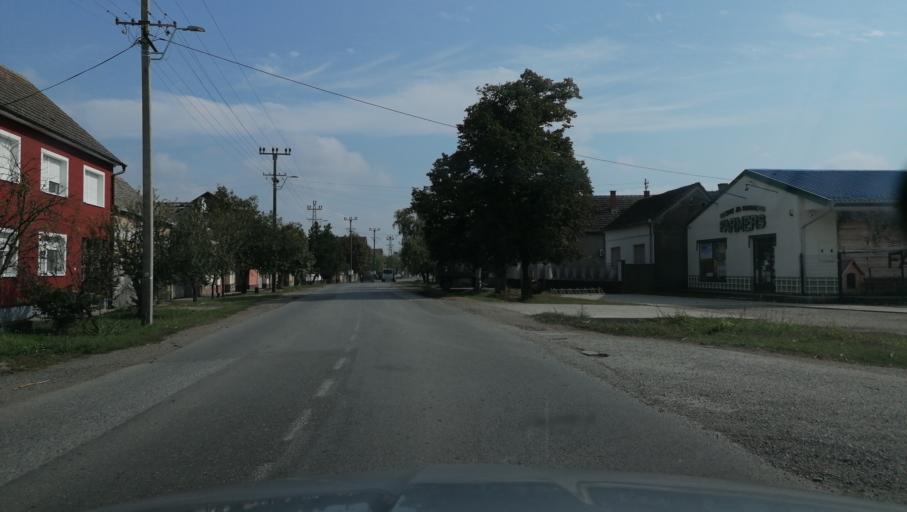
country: RS
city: Ravnje
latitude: 45.0247
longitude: 19.3972
